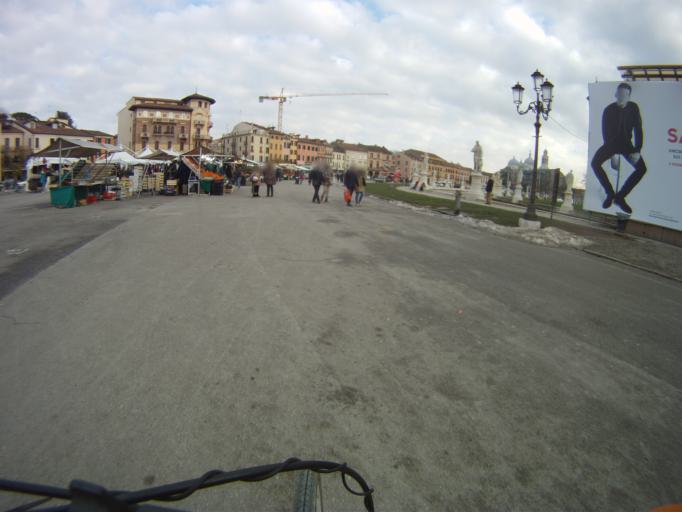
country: IT
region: Veneto
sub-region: Provincia di Padova
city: Padova
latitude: 45.3997
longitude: 11.8767
